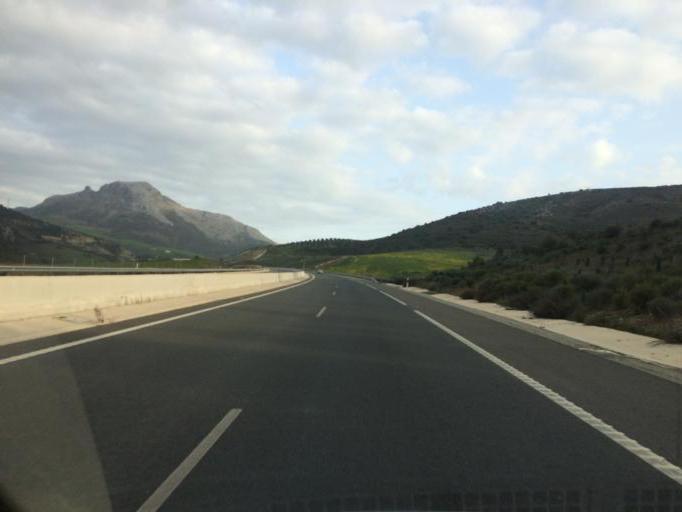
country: ES
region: Andalusia
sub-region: Provincia de Malaga
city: Casabermeja
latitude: 36.9366
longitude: -4.4319
